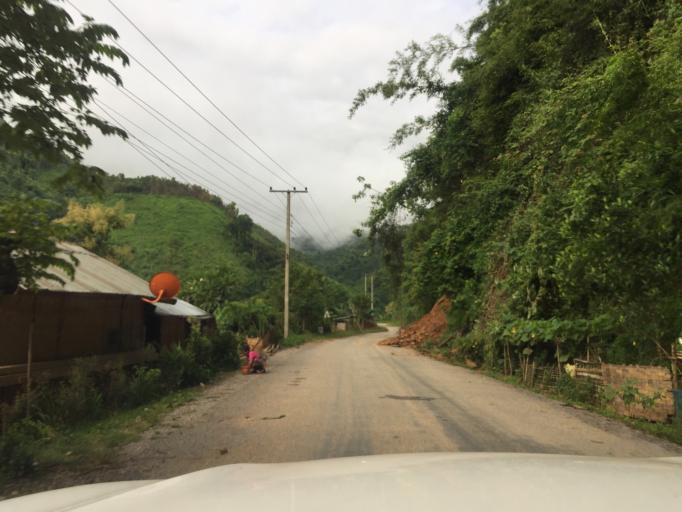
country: LA
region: Phongsali
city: Khoa
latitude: 21.1029
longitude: 102.2835
